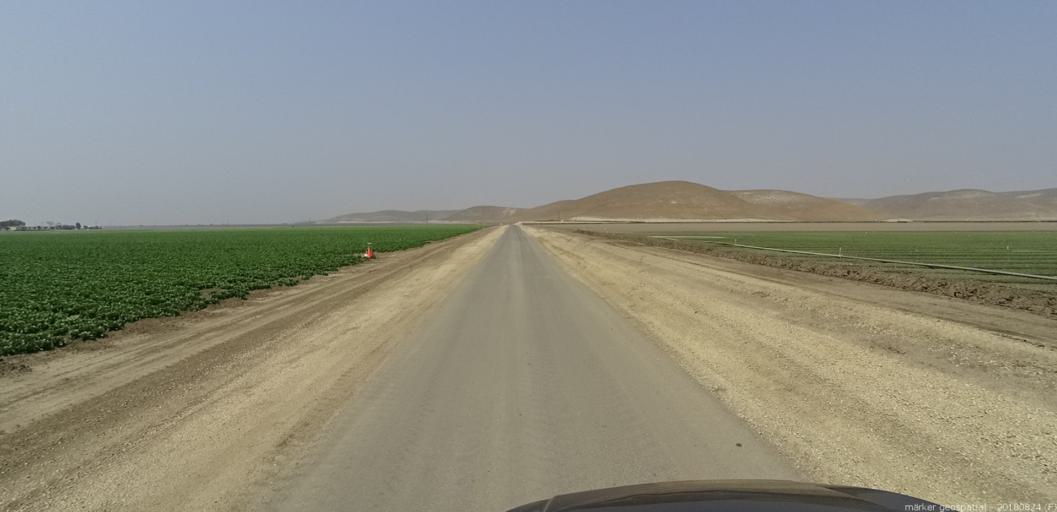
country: US
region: California
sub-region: Monterey County
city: King City
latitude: 36.1725
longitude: -121.0329
